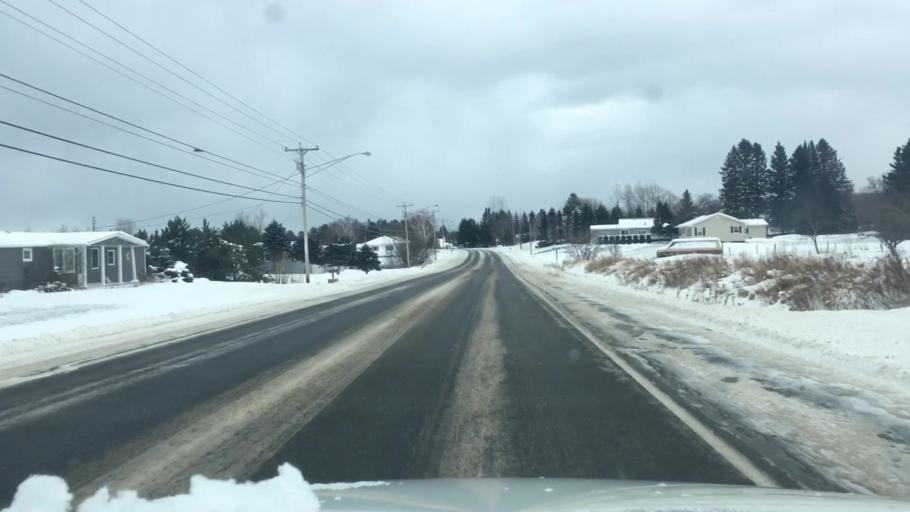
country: US
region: Maine
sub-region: Aroostook County
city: Madawaska
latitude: 47.3471
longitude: -68.2677
